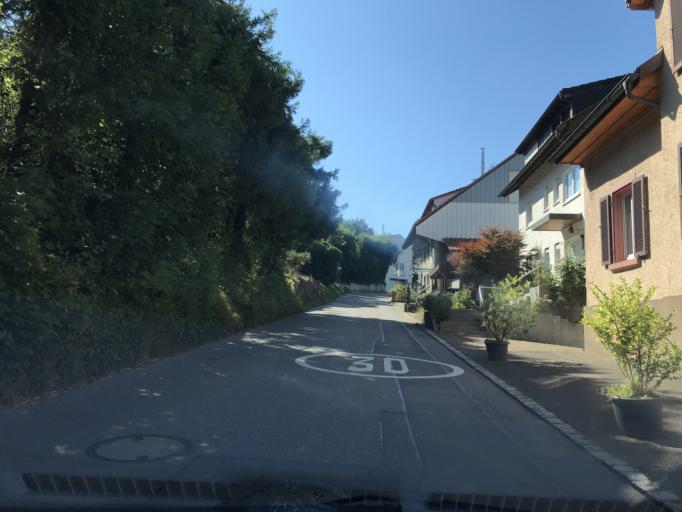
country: DE
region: Baden-Wuerttemberg
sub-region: Freiburg Region
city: Schopfheim
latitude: 47.6347
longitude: 7.8138
